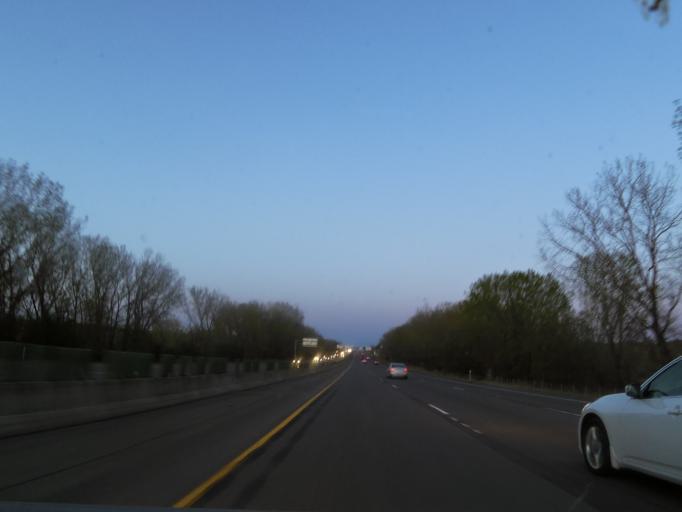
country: US
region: Minnesota
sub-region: Dakota County
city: Mendota Heights
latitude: 44.8612
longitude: -93.1845
